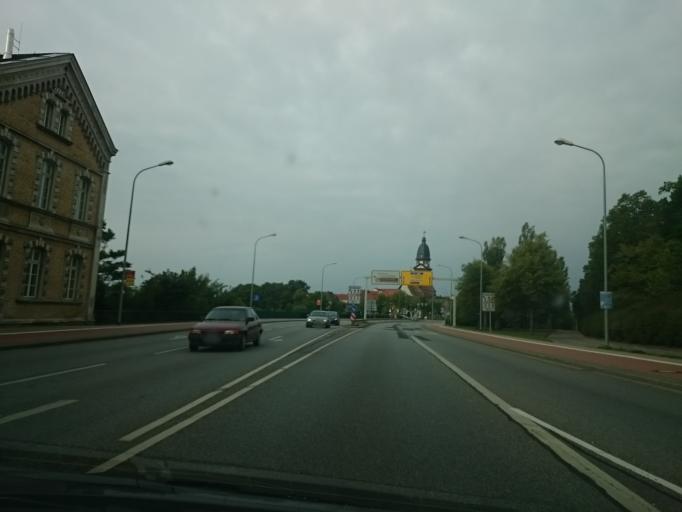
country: DE
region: Mecklenburg-Vorpommern
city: Waren
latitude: 53.5149
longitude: 12.6961
